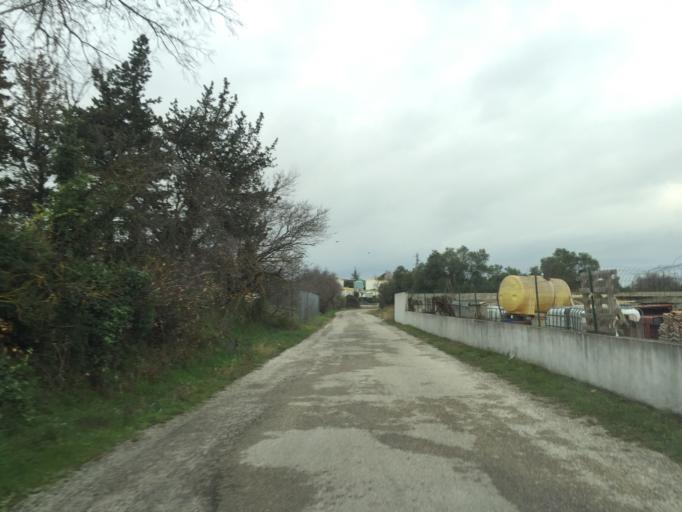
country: FR
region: Provence-Alpes-Cote d'Azur
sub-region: Departement du Vaucluse
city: Sorgues
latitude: 44.0264
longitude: 4.8744
